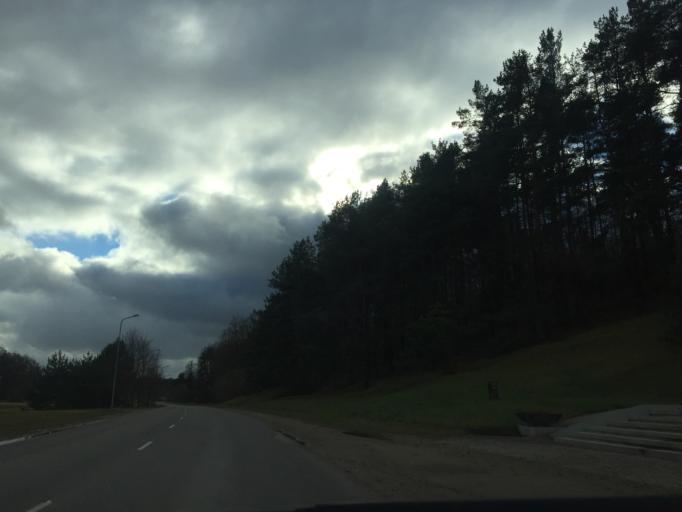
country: LV
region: Tukuma Rajons
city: Tukums
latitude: 56.9664
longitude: 23.1377
